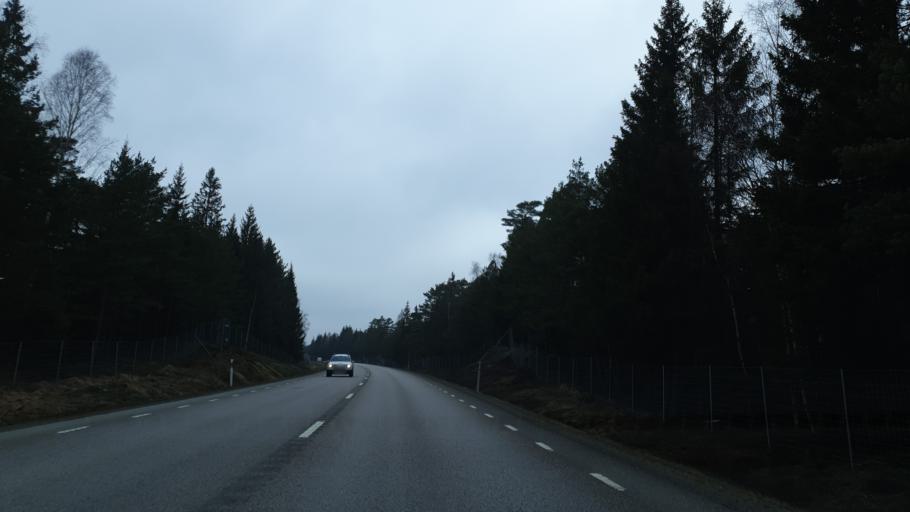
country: SE
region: Vaestra Goetaland
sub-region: Harryda Kommun
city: Hindas
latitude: 57.6647
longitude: 12.3673
